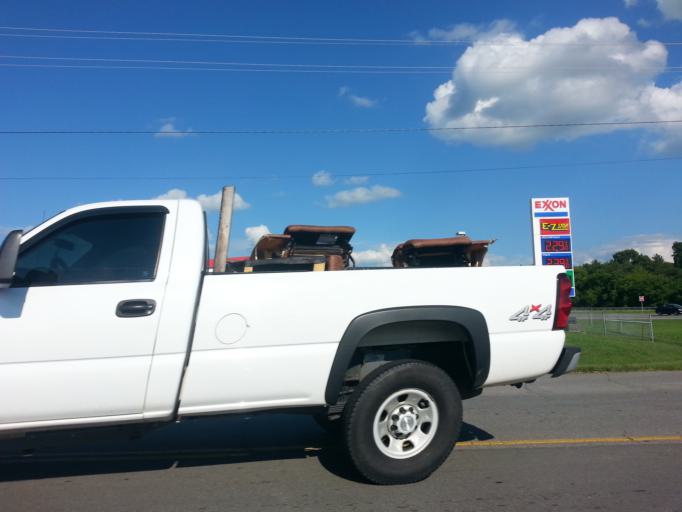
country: US
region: Tennessee
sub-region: Blount County
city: Maryville
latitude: 35.7570
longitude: -84.0346
